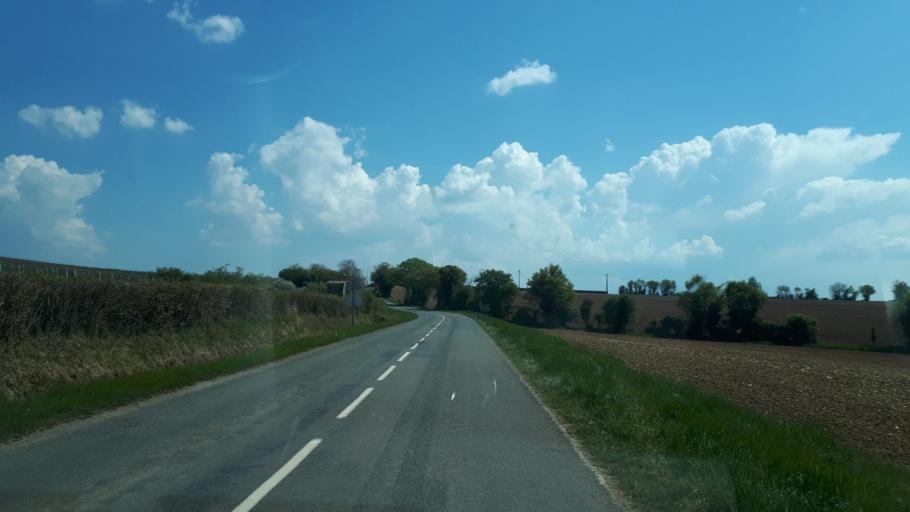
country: FR
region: Centre
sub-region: Departement du Cher
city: Sancerre
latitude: 47.3045
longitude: 2.7336
